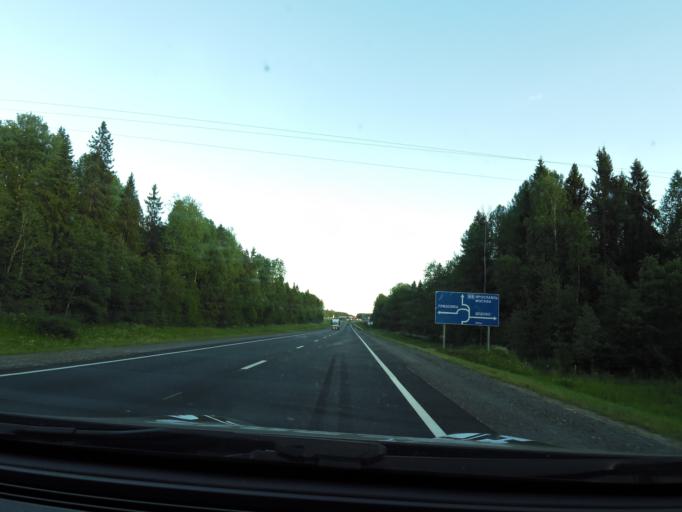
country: RU
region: Vologda
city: Gryazovets
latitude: 58.8917
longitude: 40.1878
